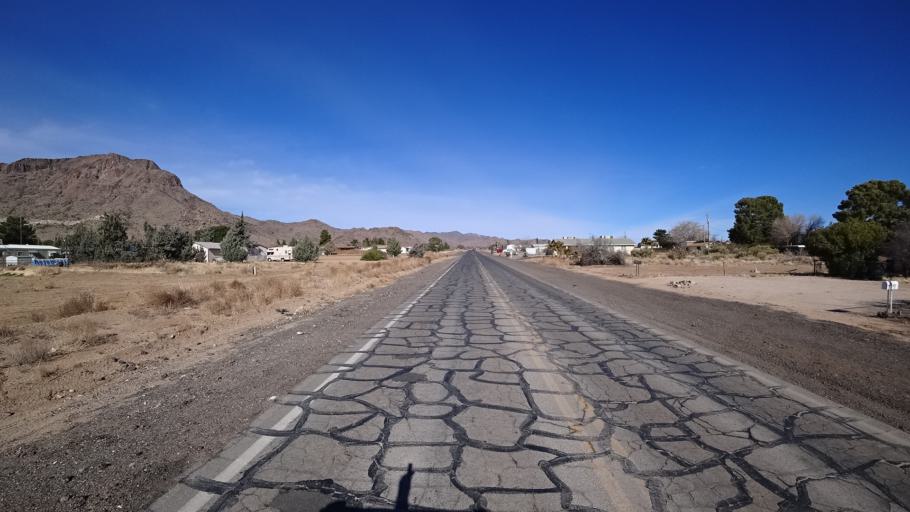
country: US
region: Arizona
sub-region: Mohave County
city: New Kingman-Butler
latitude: 35.2710
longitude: -114.0447
